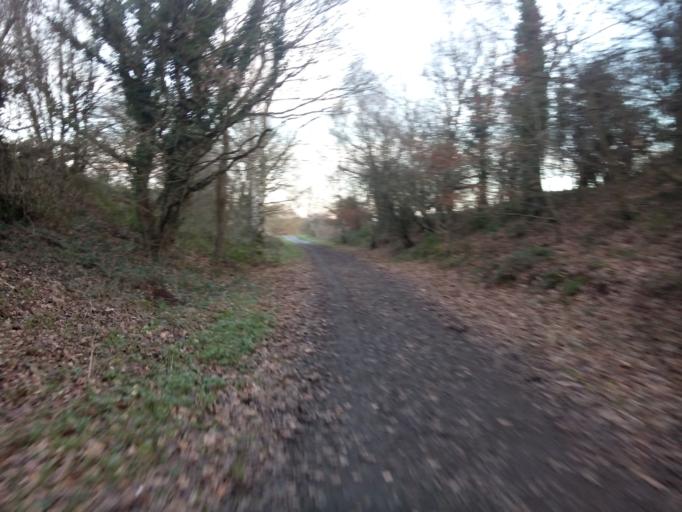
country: GB
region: England
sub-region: County Durham
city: Ushaw Moor
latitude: 54.7672
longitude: -1.6193
